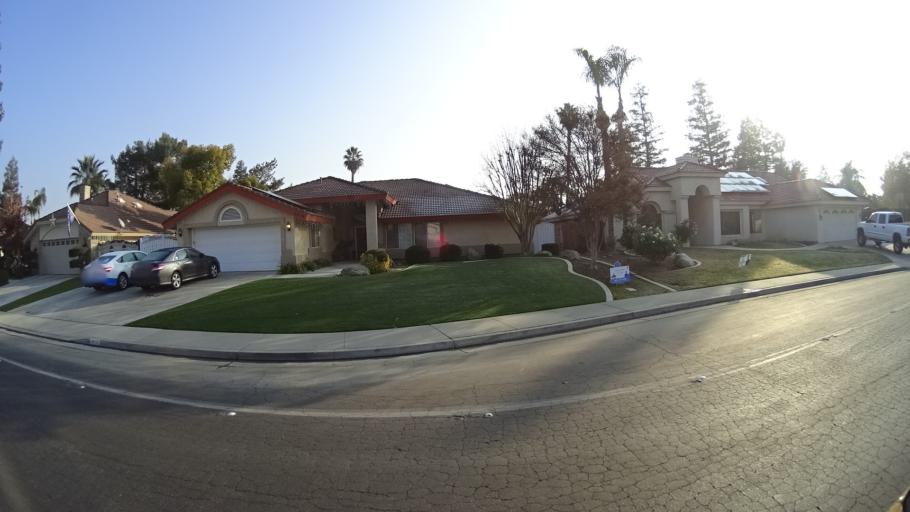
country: US
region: California
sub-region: Kern County
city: Greenacres
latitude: 35.3295
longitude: -119.1021
